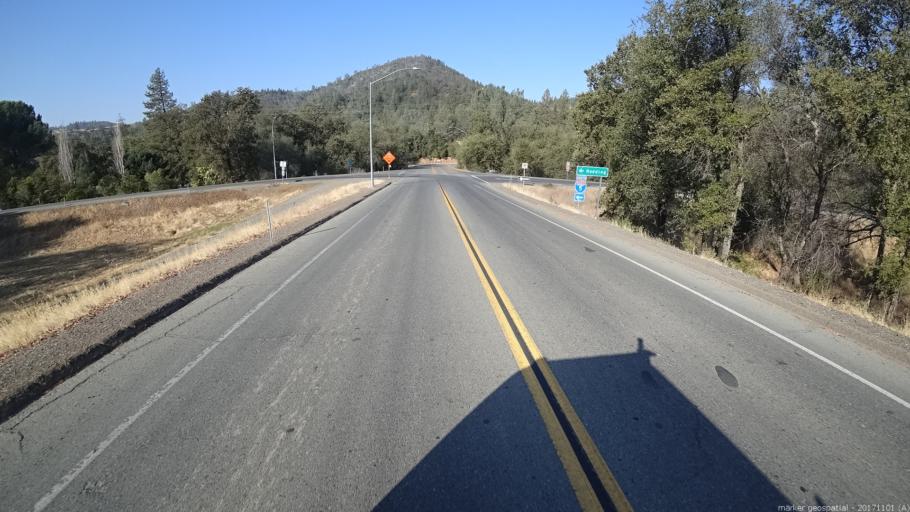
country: US
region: California
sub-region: Shasta County
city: Shasta Lake
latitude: 40.7313
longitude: -122.3212
